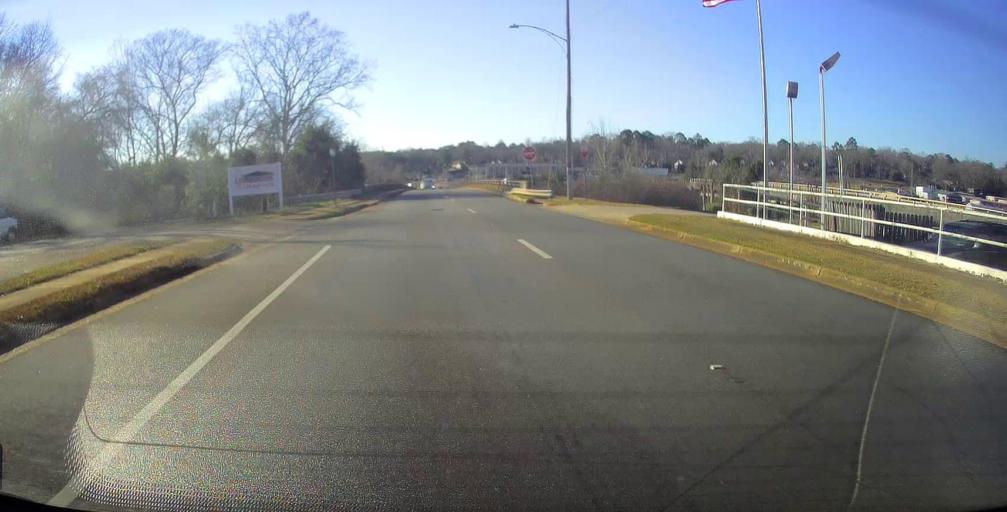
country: US
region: Georgia
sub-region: Sumter County
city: Americus
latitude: 32.0731
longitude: -84.2400
